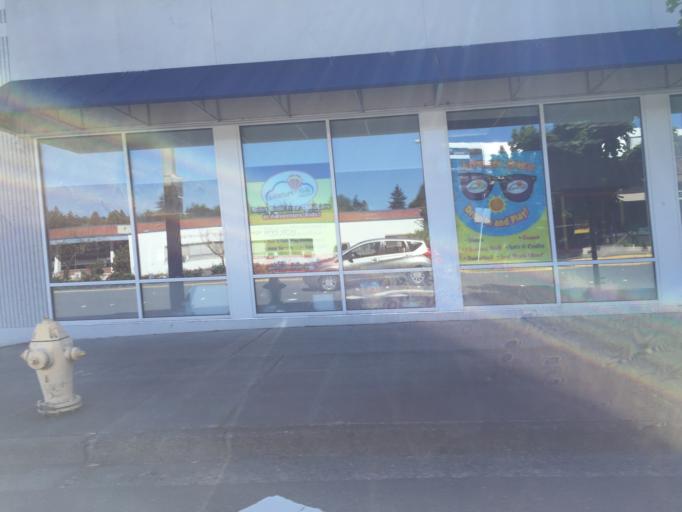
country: US
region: Washington
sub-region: King County
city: Bellevue
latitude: 47.6202
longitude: -122.2016
